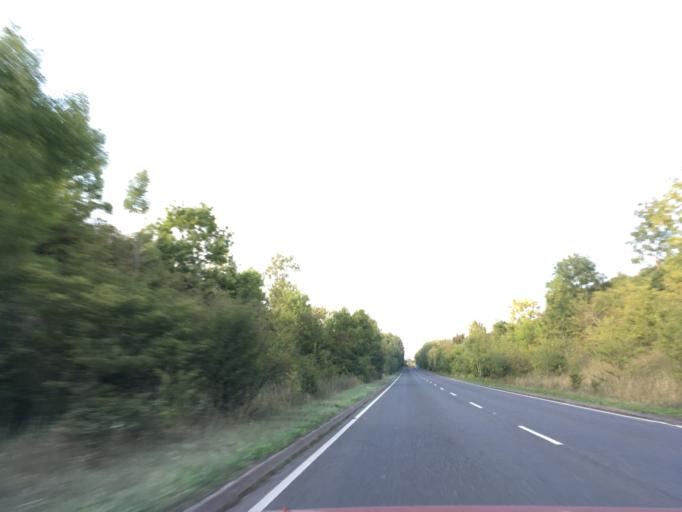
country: GB
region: England
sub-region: Warwickshire
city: Shipston on Stour
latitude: 52.0809
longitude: -1.6411
